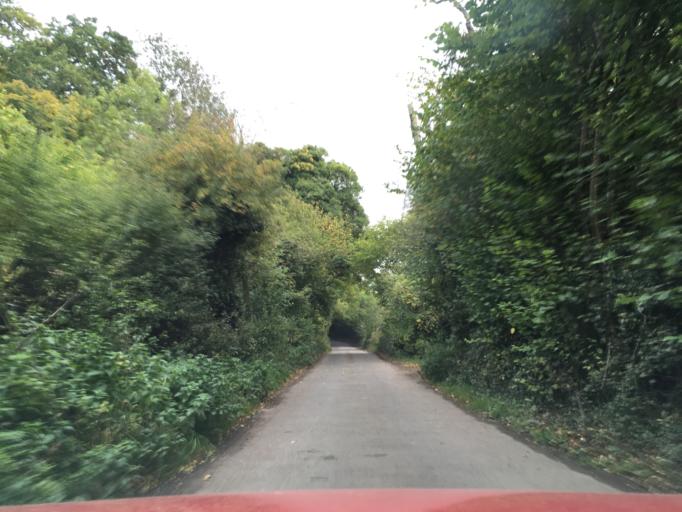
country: GB
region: England
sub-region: South Gloucestershire
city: Wickwar
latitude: 51.5987
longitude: -2.3948
